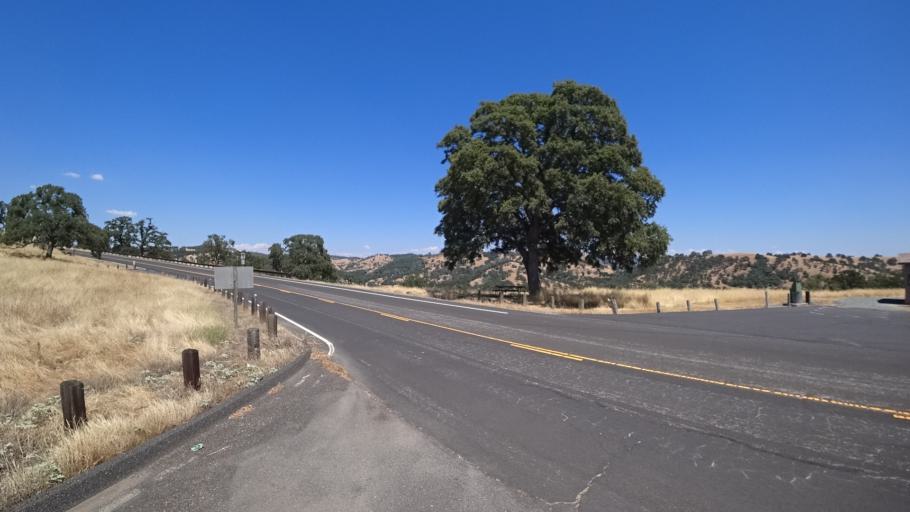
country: US
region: California
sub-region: Calaveras County
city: Angels Camp
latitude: 38.0154
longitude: -120.5255
